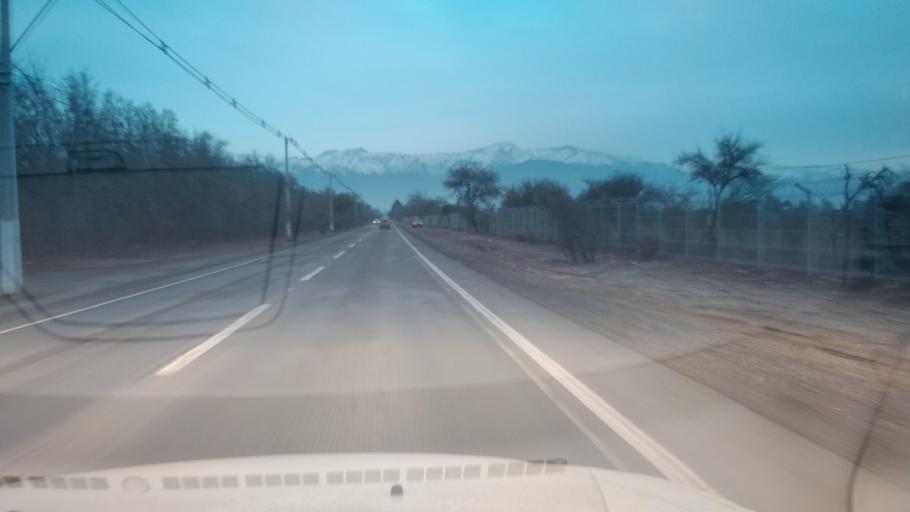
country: CL
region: Santiago Metropolitan
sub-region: Provincia de Chacabuco
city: Chicureo Abajo
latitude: -33.0929
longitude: -70.7184
